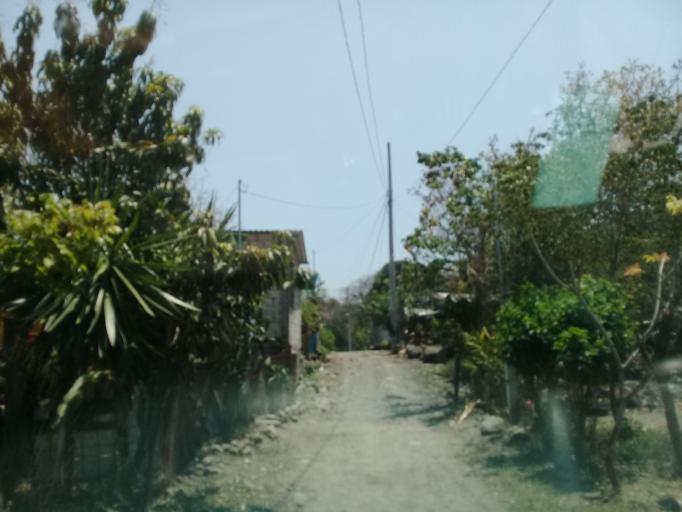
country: MX
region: Veracruz
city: Paraje Nuevo
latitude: 18.8720
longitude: -96.8677
